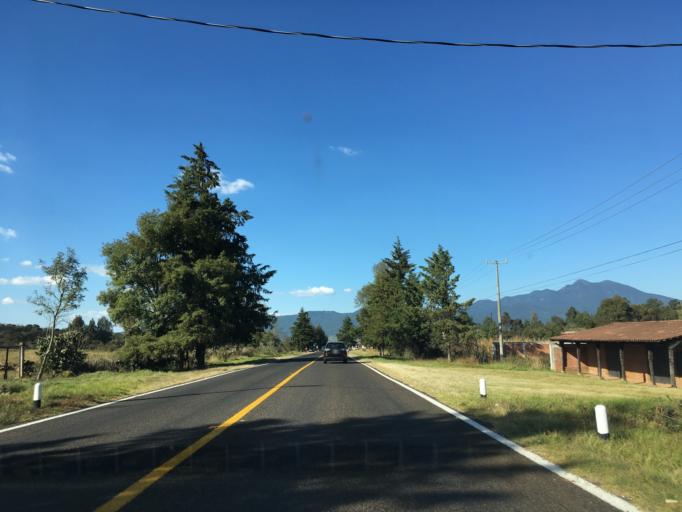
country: MX
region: Michoacan
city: Tzintzuntzan
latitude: 19.6094
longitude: -101.5768
